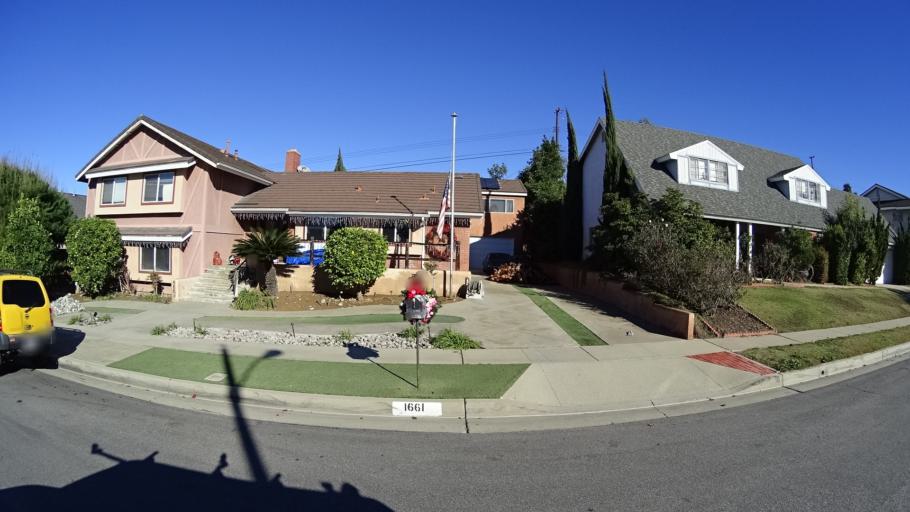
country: US
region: California
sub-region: Orange County
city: La Habra
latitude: 33.9432
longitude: -117.9279
